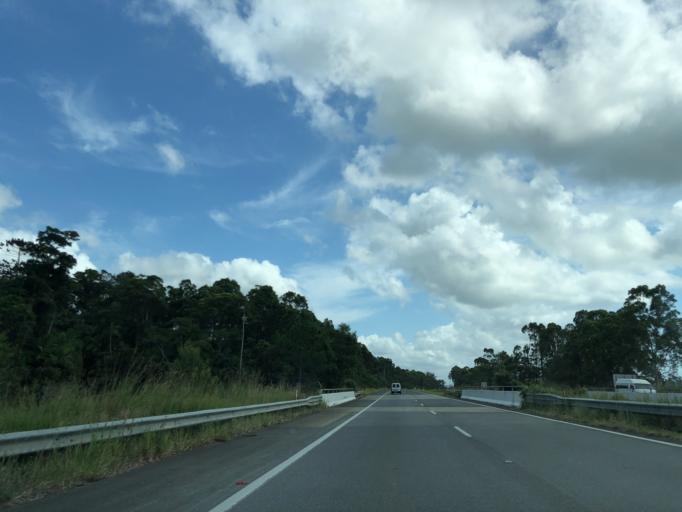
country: AU
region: New South Wales
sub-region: Tweed
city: Pottsville Beach
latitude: -28.3688
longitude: 153.5234
